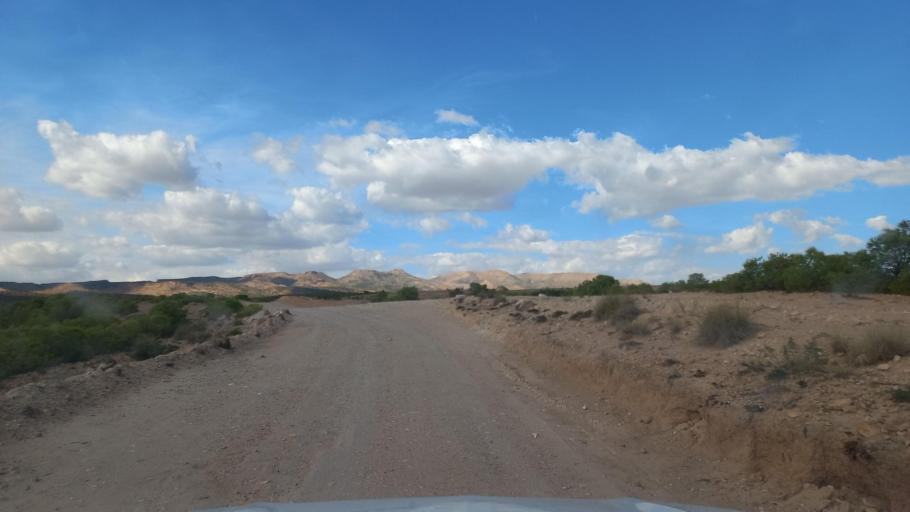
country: TN
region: Al Qasrayn
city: Sbiba
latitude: 35.3989
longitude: 9.0115
